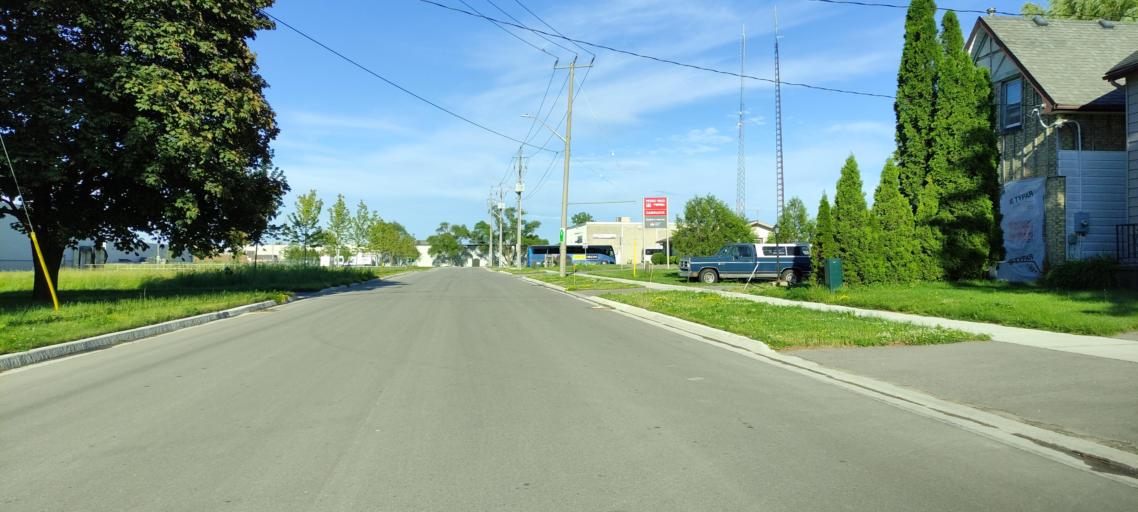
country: CA
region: Ontario
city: Stratford
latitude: 43.3653
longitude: -80.9599
